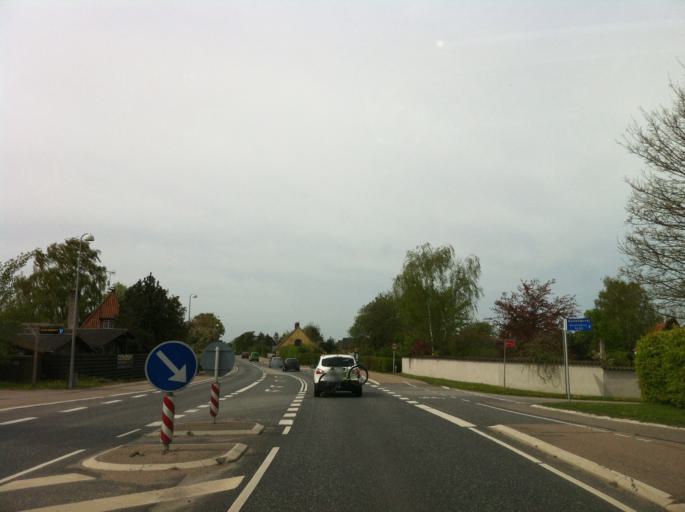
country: DK
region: Capital Region
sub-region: Hillerod Kommune
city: Hillerod
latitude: 55.9027
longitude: 12.2428
